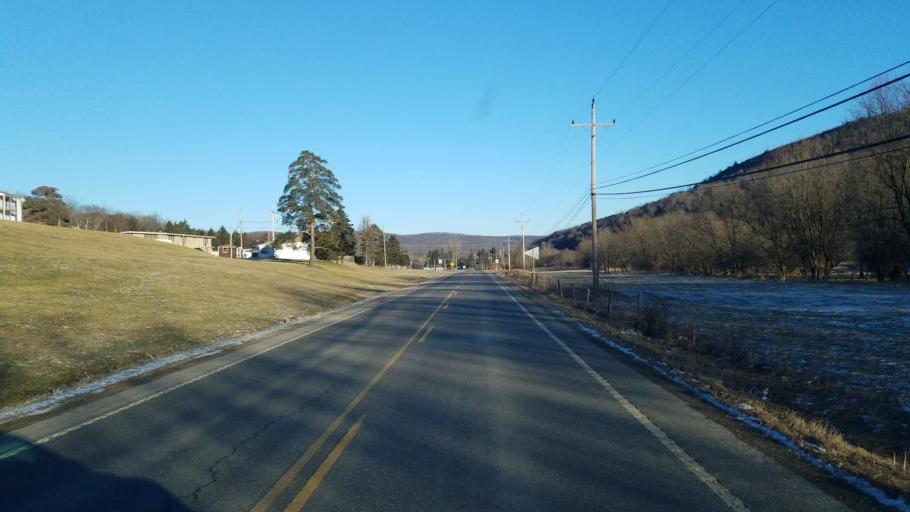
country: US
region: Pennsylvania
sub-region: Tioga County
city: Westfield
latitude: 41.9427
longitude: -77.6637
